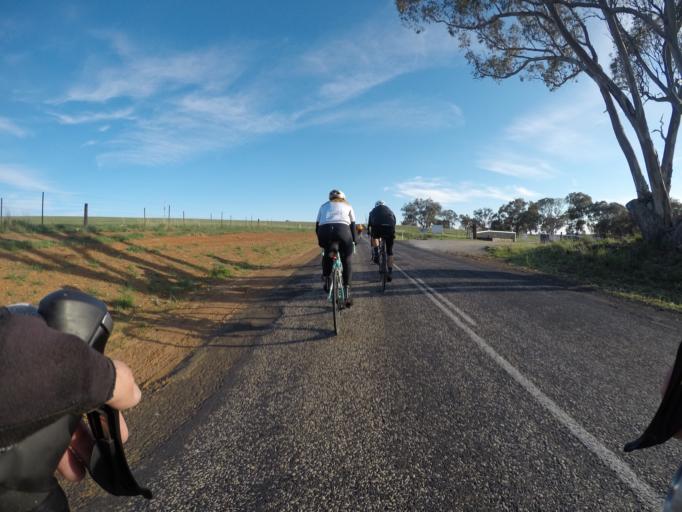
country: AU
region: New South Wales
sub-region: Cabonne
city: Molong
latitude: -32.9931
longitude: 148.7877
